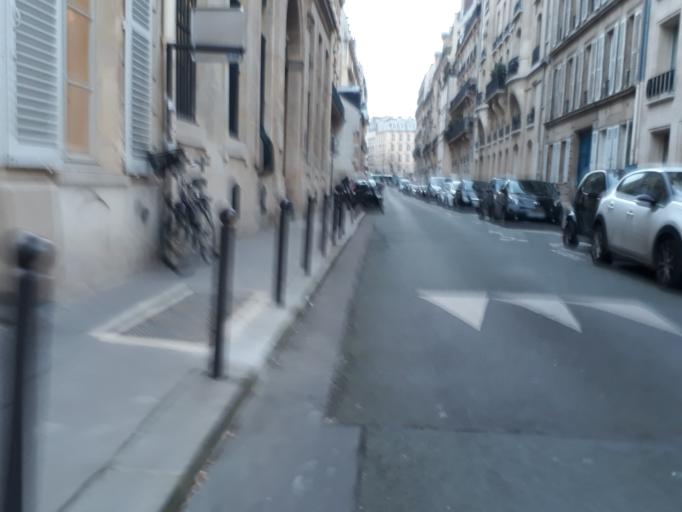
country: FR
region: Ile-de-France
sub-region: Paris
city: Paris
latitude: 48.8490
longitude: 2.3269
